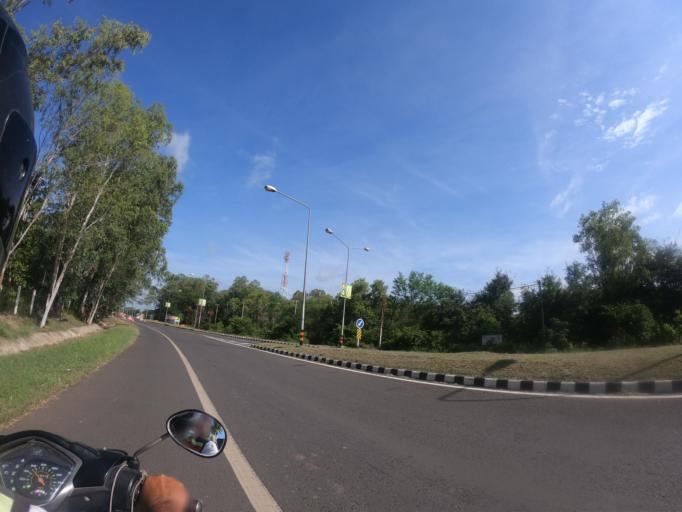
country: TH
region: Surin
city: Kap Choeng
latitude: 14.4512
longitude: 103.6983
